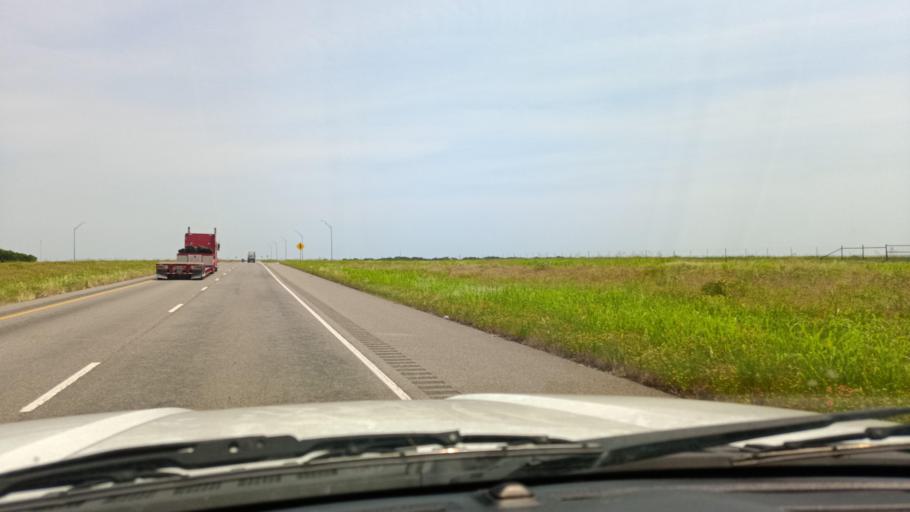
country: US
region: Texas
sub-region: Bell County
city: Little River-Academy
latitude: 31.0202
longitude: -97.3120
